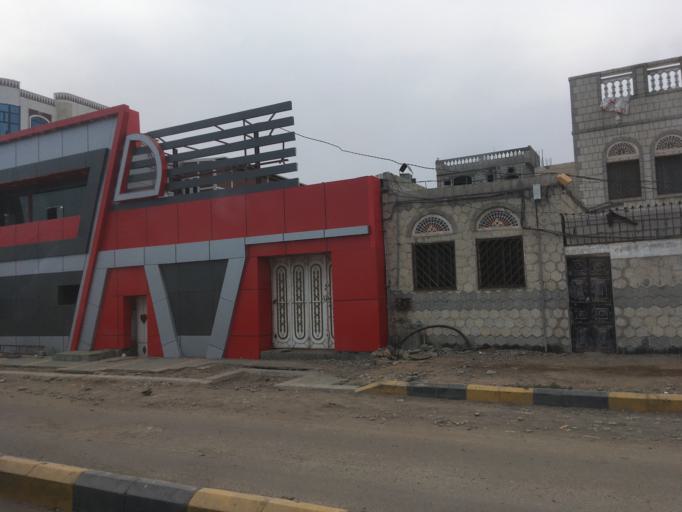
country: YE
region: Aden
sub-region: Al Mansura
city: Al Mansurah
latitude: 12.8567
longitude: 44.9950
